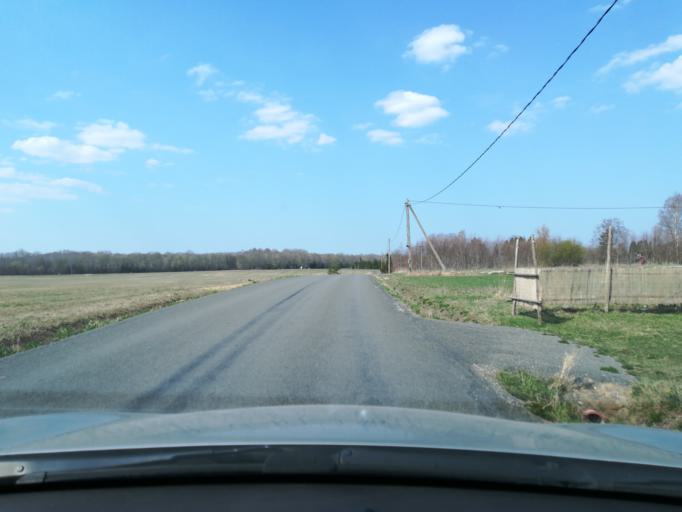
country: EE
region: Harju
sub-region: Saue linn
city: Saue
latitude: 59.3598
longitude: 24.5612
